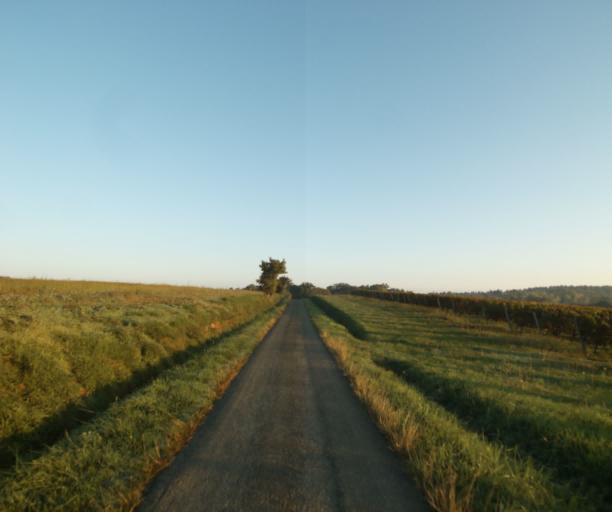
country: FR
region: Midi-Pyrenees
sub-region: Departement du Gers
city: Eauze
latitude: 43.7895
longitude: 0.1789
